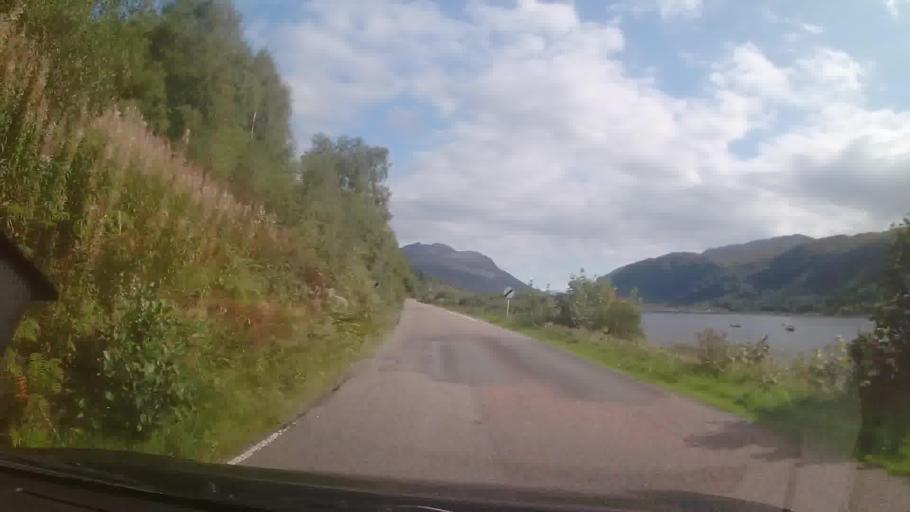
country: GB
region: Scotland
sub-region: Argyll and Bute
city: Oban
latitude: 56.6874
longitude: -5.5594
